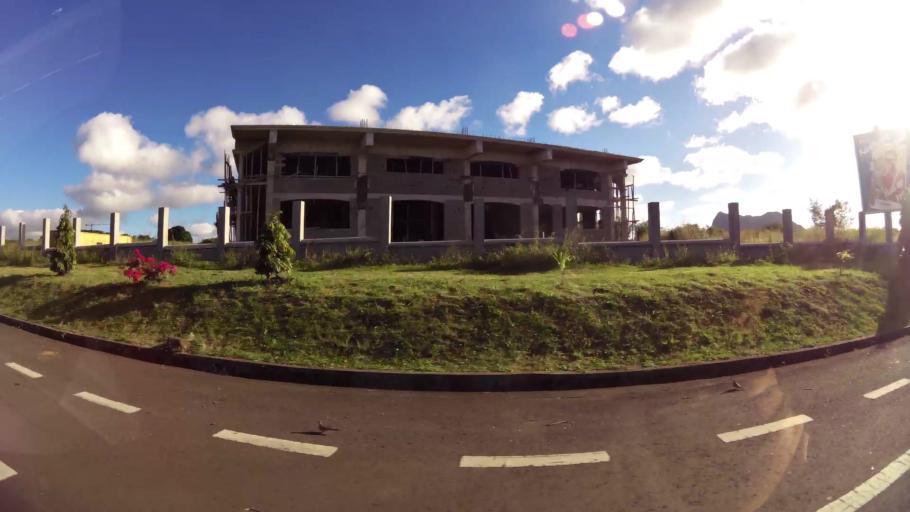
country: MU
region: Plaines Wilhems
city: Quatre Bornes
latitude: -20.2694
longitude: 57.4949
